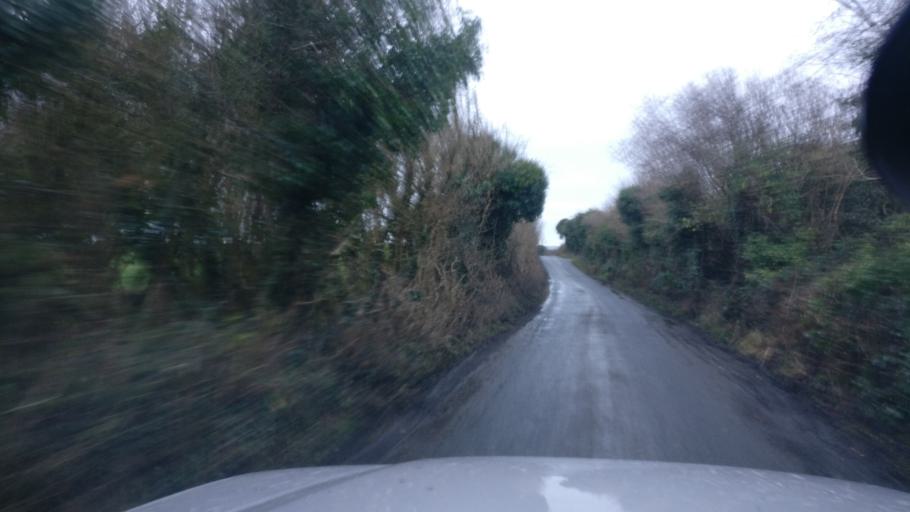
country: IE
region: Connaught
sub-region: County Galway
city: Loughrea
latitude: 53.2083
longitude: -8.6655
